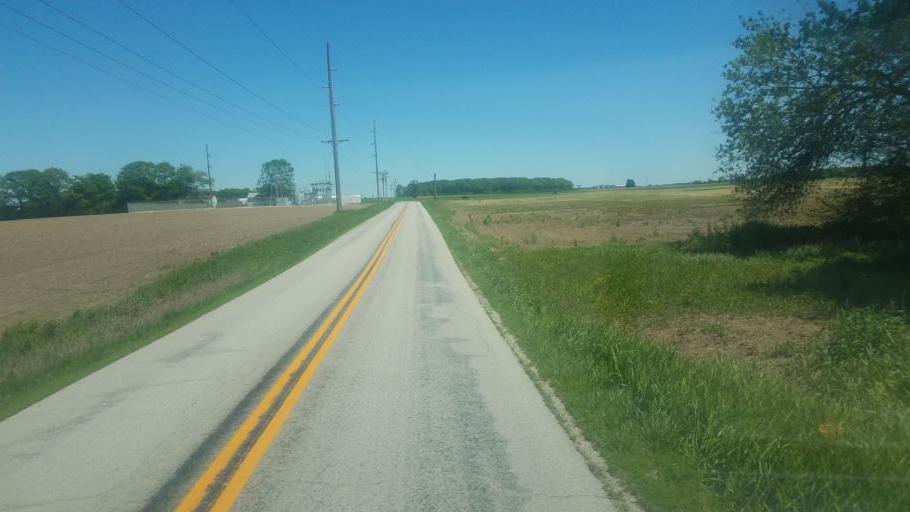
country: US
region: Ohio
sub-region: Miami County
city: Covington
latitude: 40.2273
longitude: -84.3238
